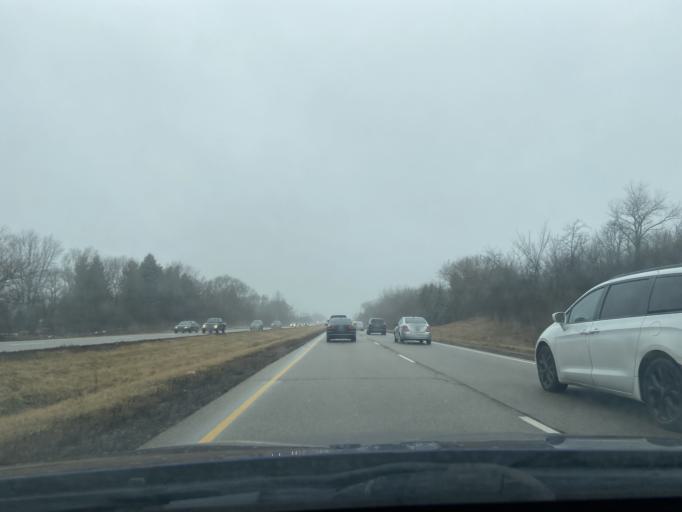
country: US
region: Illinois
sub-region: Lake County
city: Wauconda
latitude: 42.2468
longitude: -88.1298
